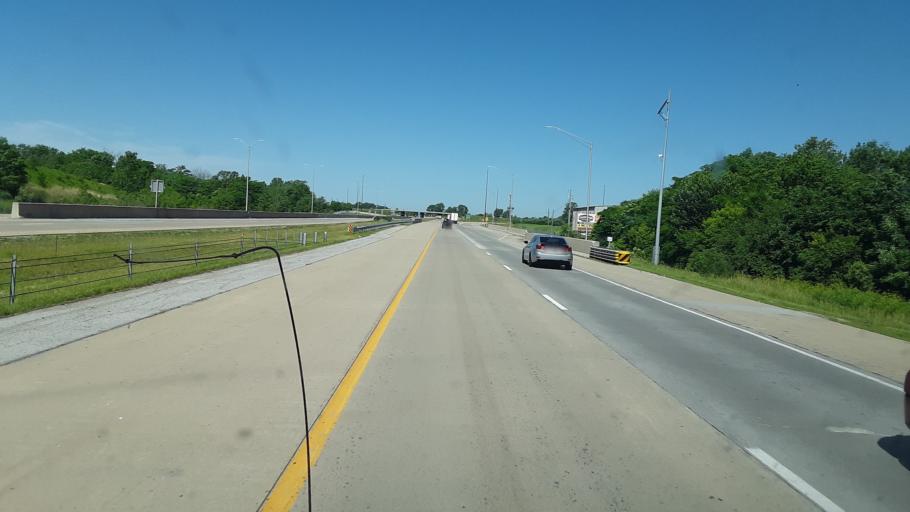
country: US
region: Indiana
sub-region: Marion County
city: Cumberland
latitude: 39.8196
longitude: -85.9042
